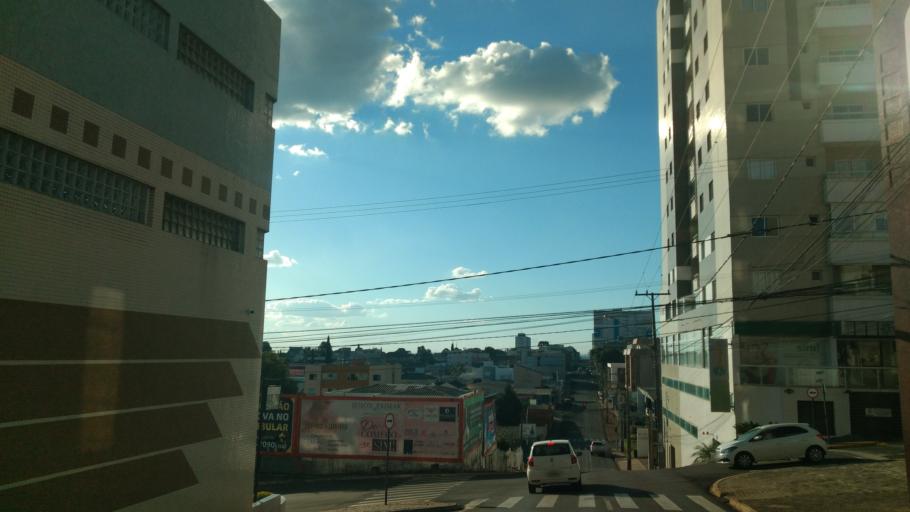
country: BR
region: Parana
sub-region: Guarapuava
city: Guarapuava
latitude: -25.3967
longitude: -51.4694
